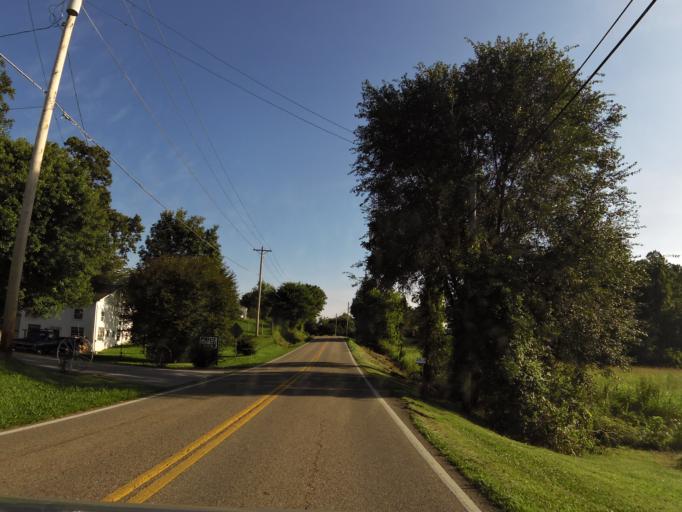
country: US
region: Tennessee
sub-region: Blount County
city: Maryville
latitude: 35.6843
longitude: -83.9731
